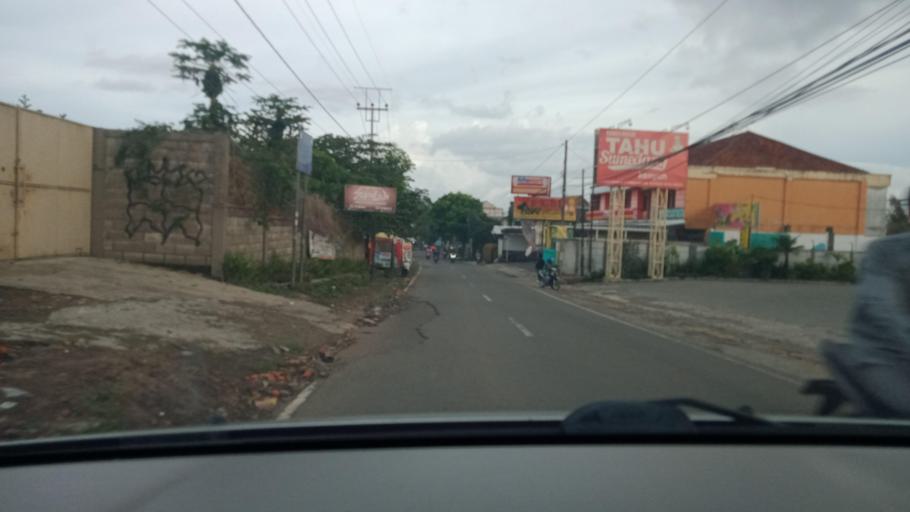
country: ID
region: West Java
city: Lembang
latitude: -6.8054
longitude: 107.5940
